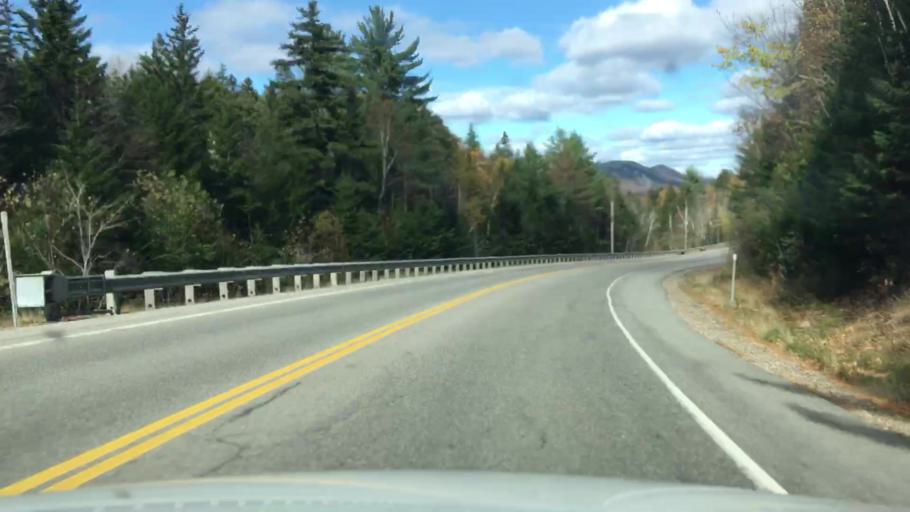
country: US
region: New Hampshire
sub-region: Coos County
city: Gorham
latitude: 44.3070
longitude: -71.2206
